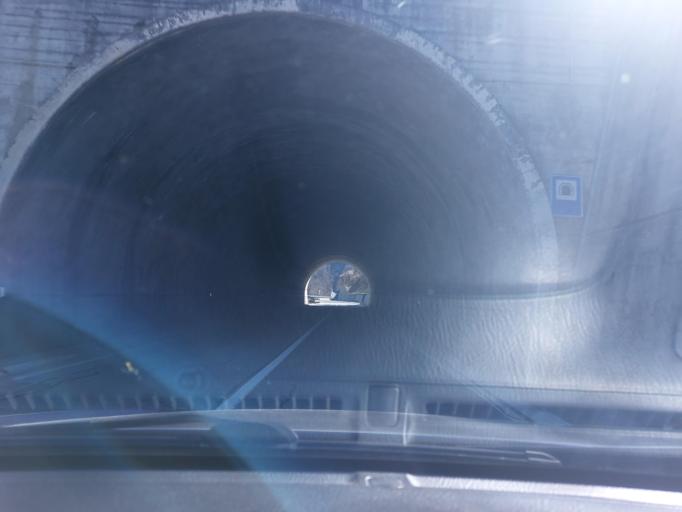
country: CH
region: Valais
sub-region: Herens District
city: Heremence
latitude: 46.1775
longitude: 7.4110
